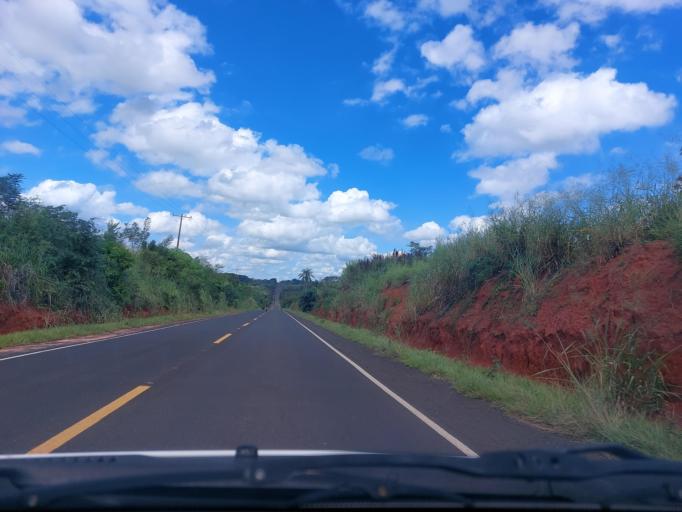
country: PY
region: San Pedro
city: Guayaybi
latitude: -24.5429
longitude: -56.5196
